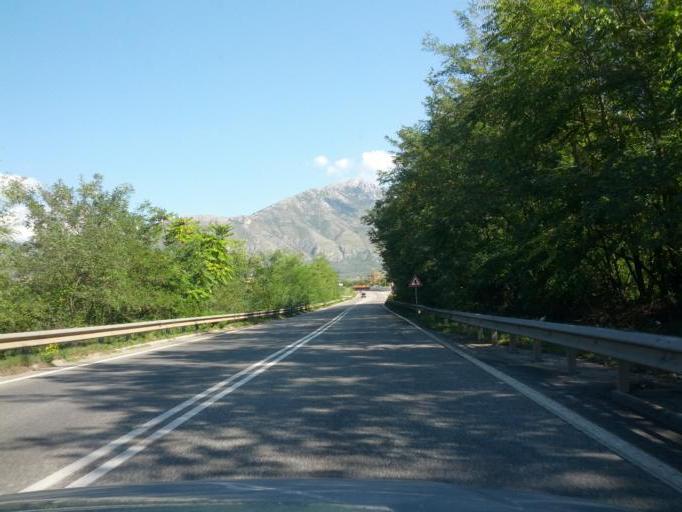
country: IT
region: Latium
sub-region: Provincia di Frosinone
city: San Vittore del Lazio
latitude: 41.4400
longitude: 13.9077
